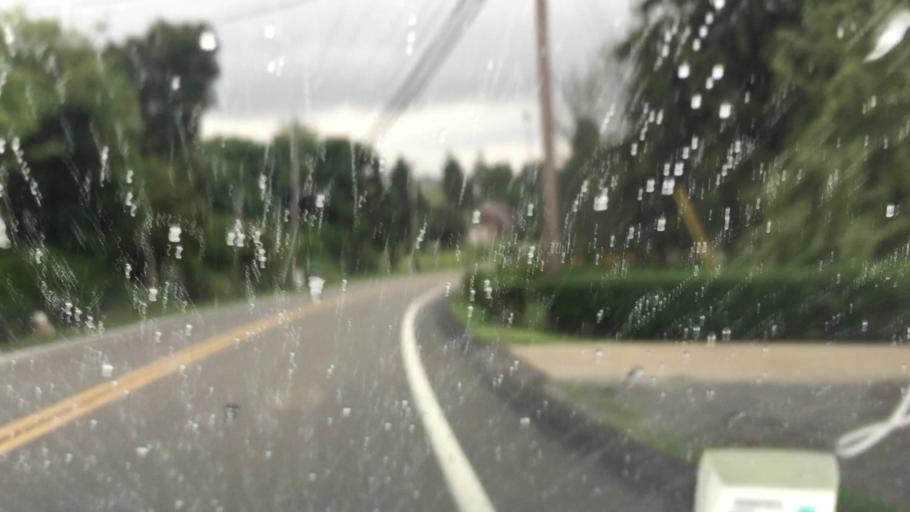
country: US
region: Pennsylvania
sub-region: Allegheny County
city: Franklin Park
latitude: 40.5674
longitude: -80.1026
